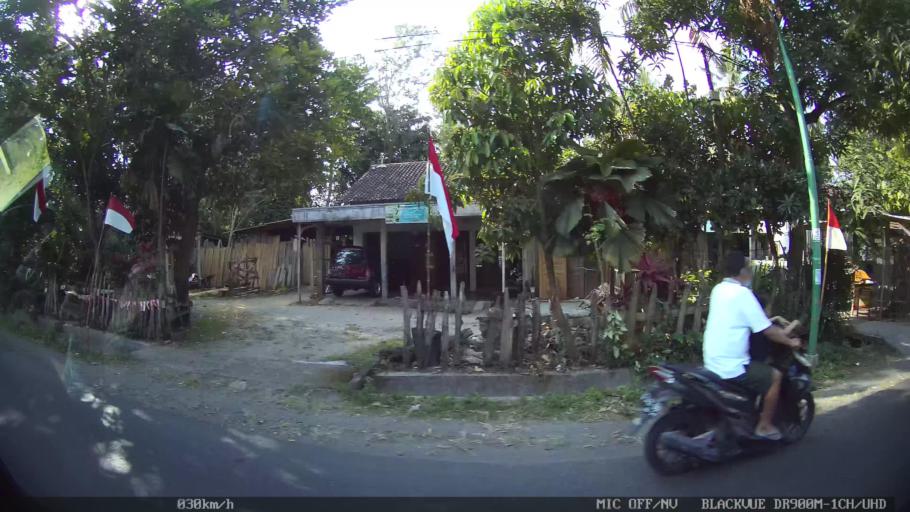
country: ID
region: Daerah Istimewa Yogyakarta
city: Pandak
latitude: -7.8928
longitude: 110.3011
